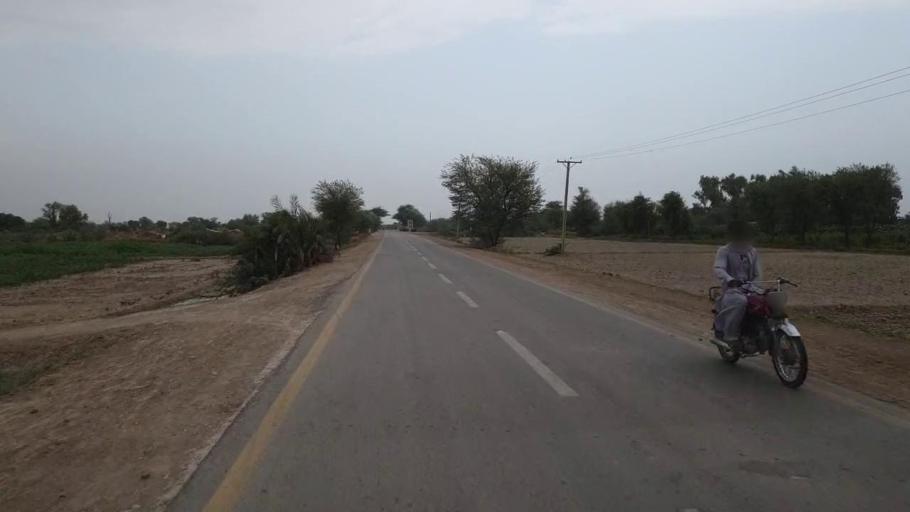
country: PK
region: Sindh
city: Bandhi
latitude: 26.5903
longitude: 68.2039
